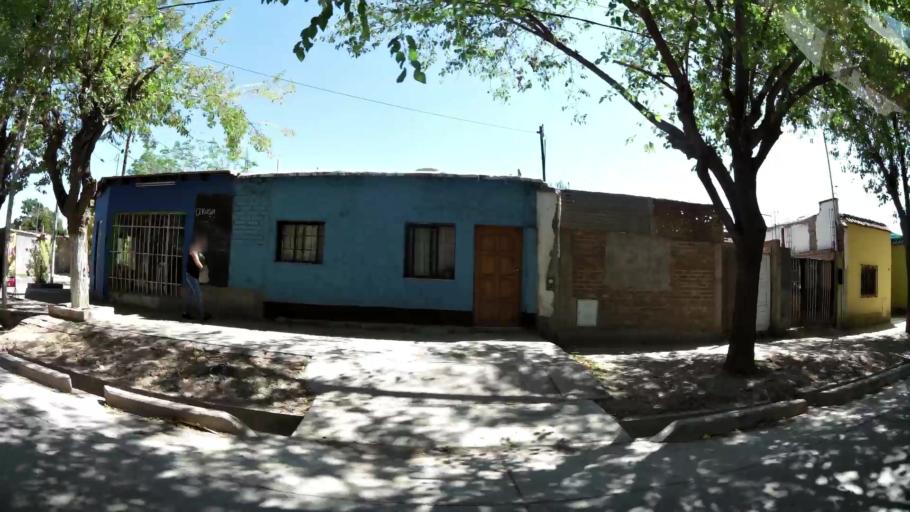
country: AR
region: Mendoza
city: Mendoza
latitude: -32.8782
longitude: -68.8208
